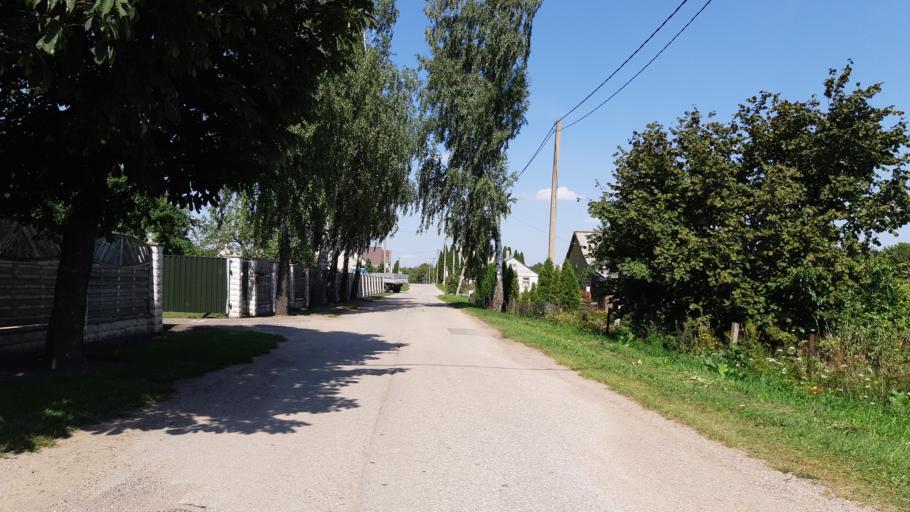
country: LT
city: Virbalis
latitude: 54.6227
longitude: 22.8176
